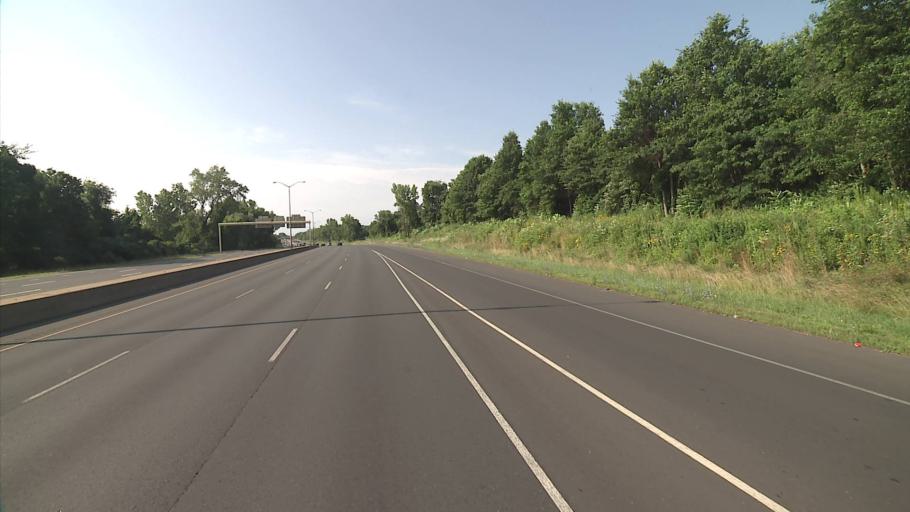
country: US
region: Connecticut
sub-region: Hartford County
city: Enfield
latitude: 41.9866
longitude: -72.5886
